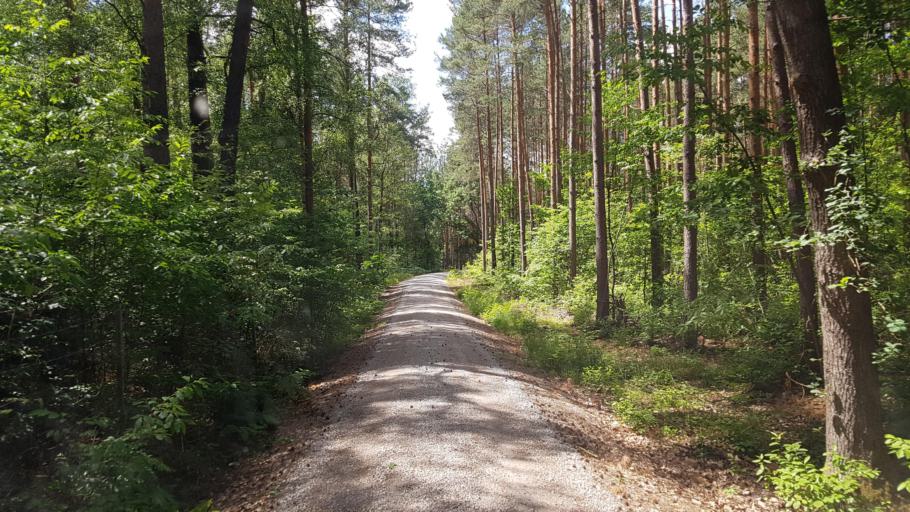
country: DE
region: Brandenburg
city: Plessa
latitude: 51.4954
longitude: 13.5974
